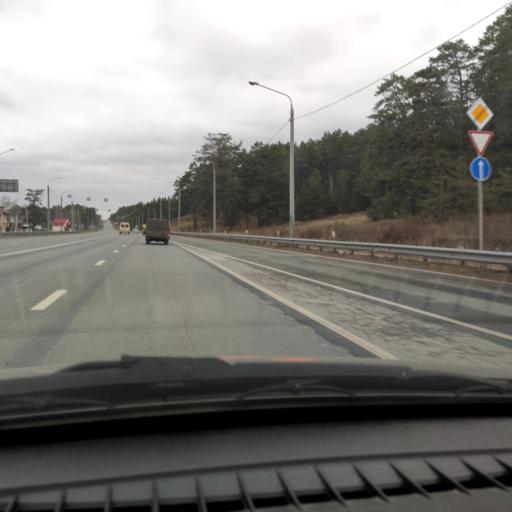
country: RU
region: Samara
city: Volzhskiy
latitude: 53.4362
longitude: 50.1128
